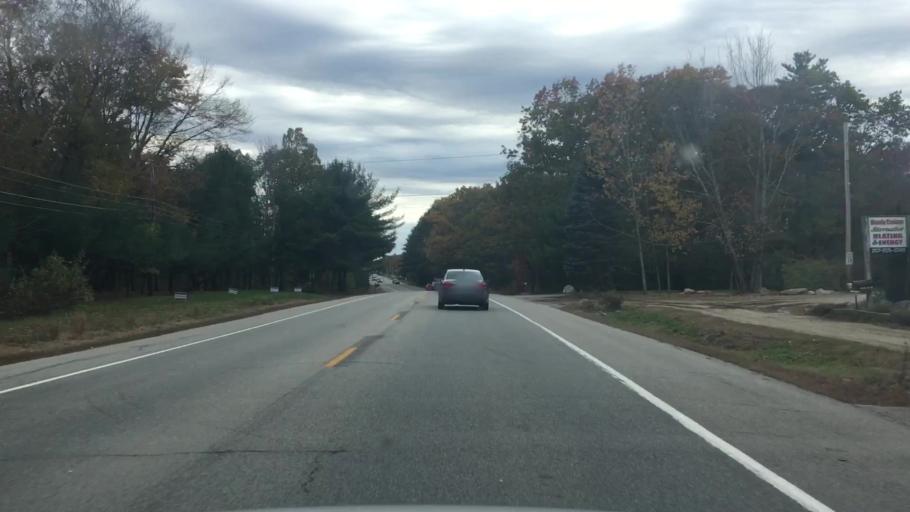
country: US
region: Maine
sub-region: York County
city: West Kennebunk
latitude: 43.4796
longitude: -70.5959
